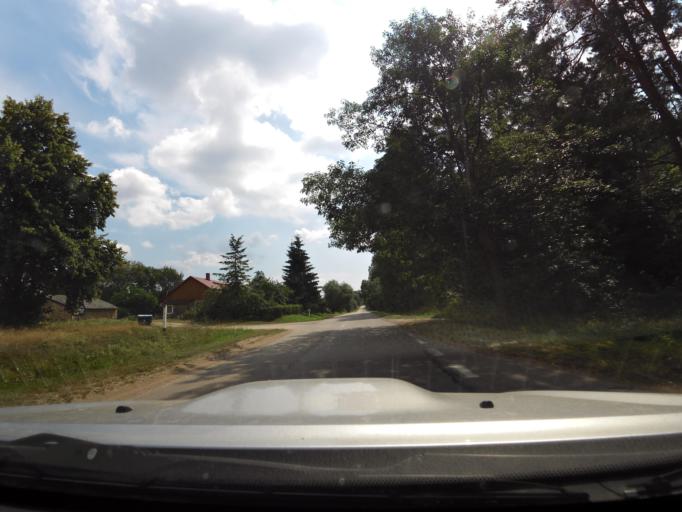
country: RU
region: Kaliningrad
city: Neman
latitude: 55.0976
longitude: 22.0175
